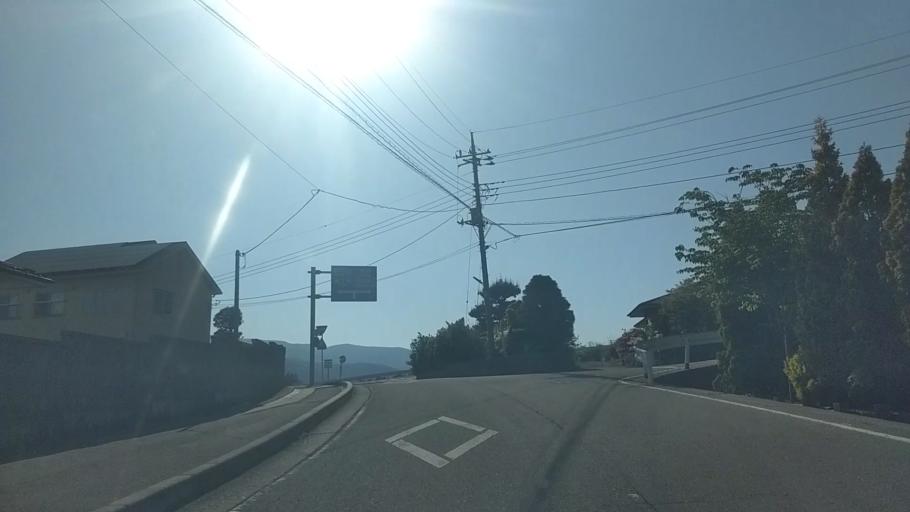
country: JP
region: Nagano
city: Chino
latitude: 35.8639
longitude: 138.3124
